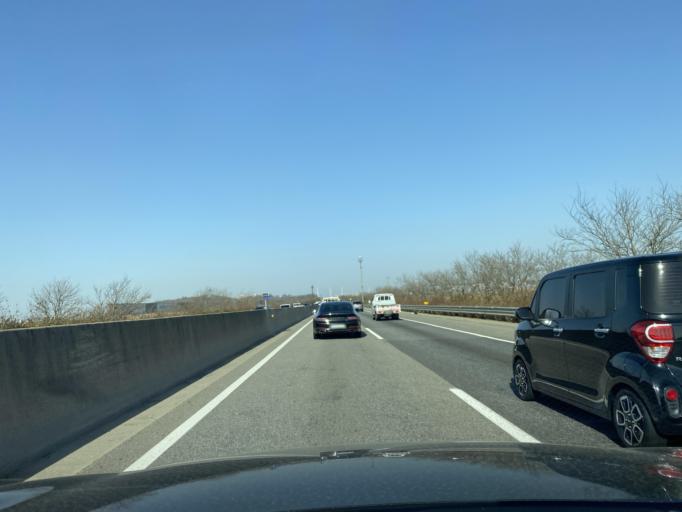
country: KR
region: Gyeonggi-do
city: Hwaseong-si
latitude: 37.2644
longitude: 126.7458
